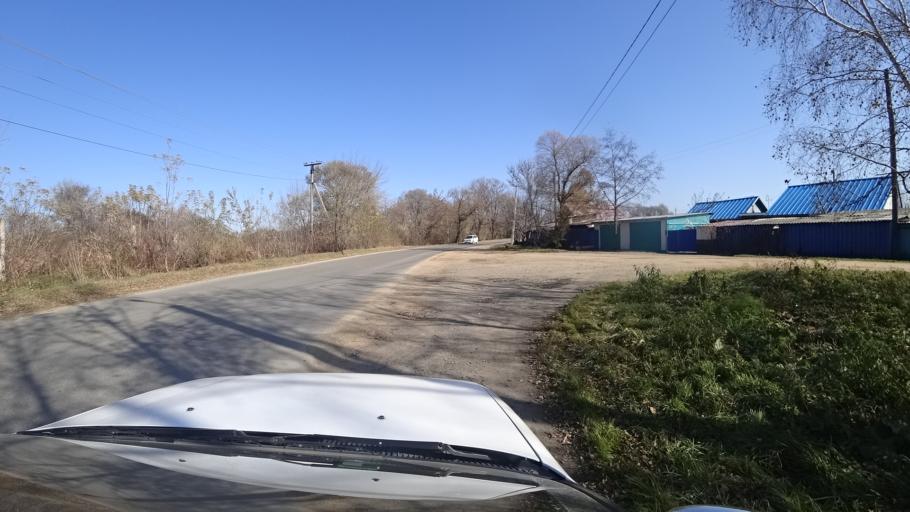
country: RU
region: Primorskiy
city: Dal'nerechensk
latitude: 45.9328
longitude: 133.7526
